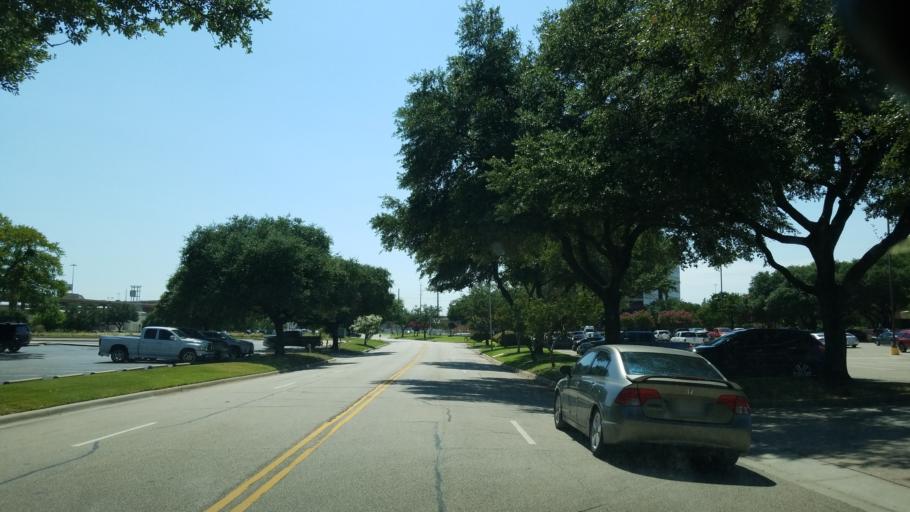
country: US
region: Texas
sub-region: Dallas County
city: Farmers Branch
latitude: 32.9116
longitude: -96.8891
